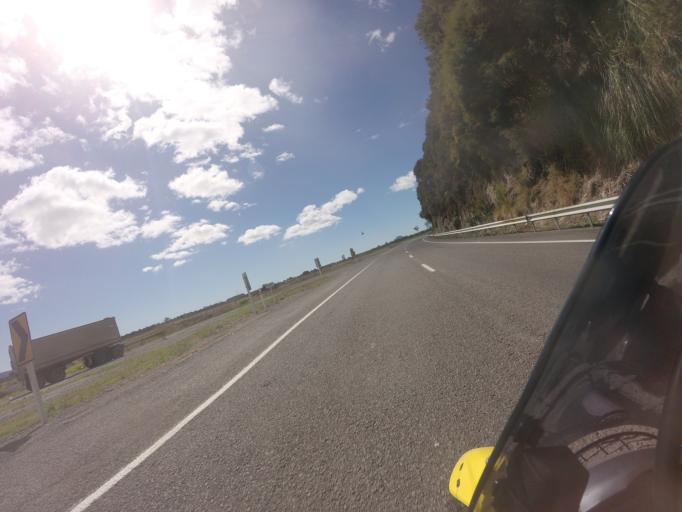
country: NZ
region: Bay of Plenty
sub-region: Whakatane District
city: Edgecumbe
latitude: -38.0078
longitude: 176.8573
